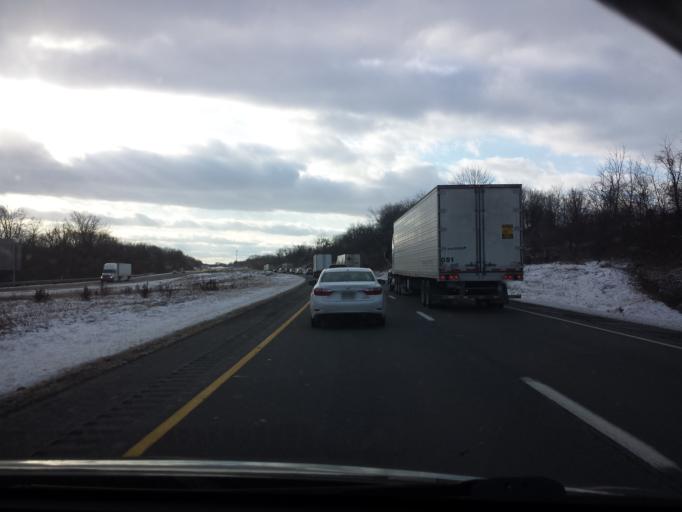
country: US
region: Pennsylvania
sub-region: Columbia County
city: Almedia
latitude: 41.0391
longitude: -76.3596
